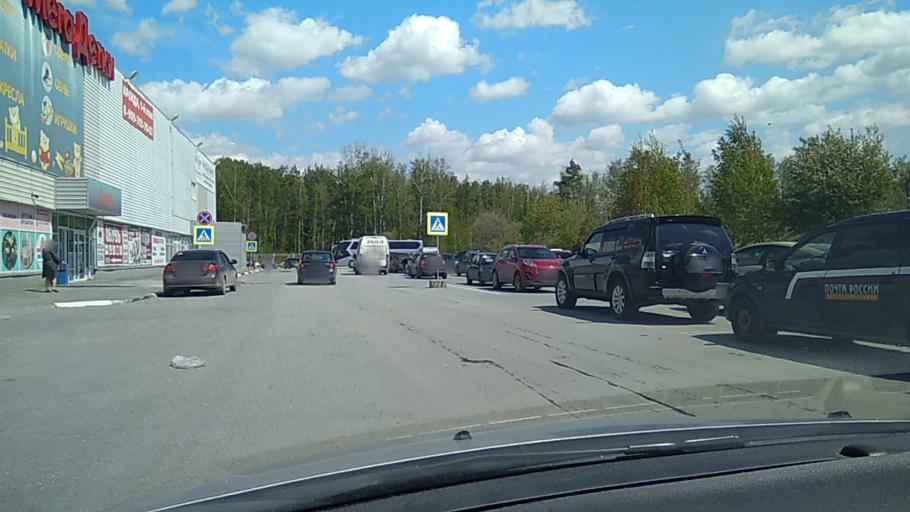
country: RU
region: Sverdlovsk
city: Istok
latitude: 56.7557
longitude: 60.7582
